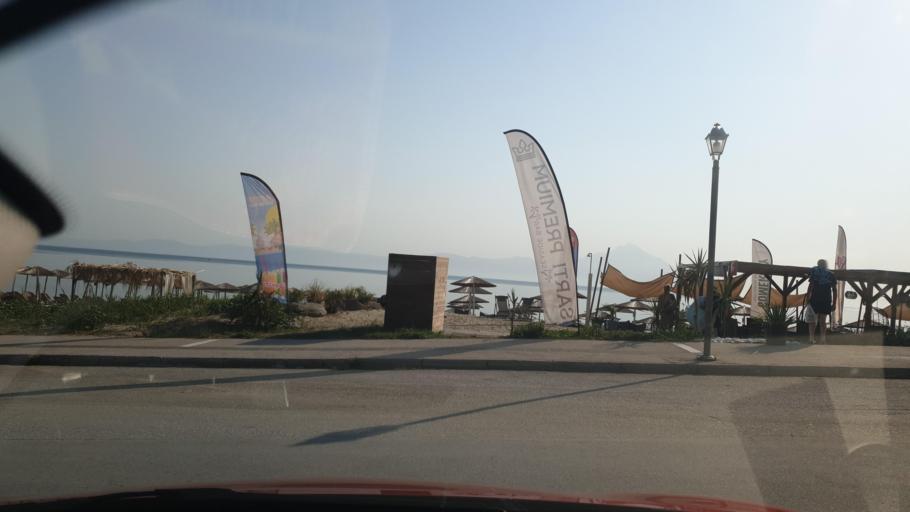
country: GR
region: Central Macedonia
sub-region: Nomos Chalkidikis
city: Sarti
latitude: 40.0821
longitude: 23.9796
